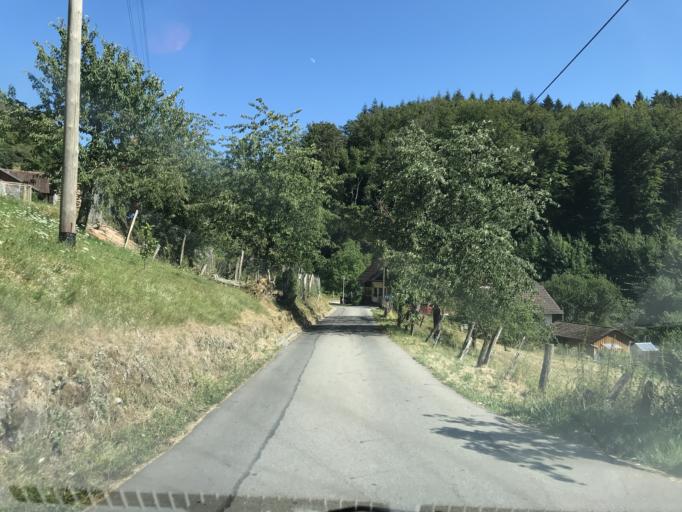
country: DE
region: Baden-Wuerttemberg
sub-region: Freiburg Region
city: Hasel
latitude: 47.6733
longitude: 7.8825
